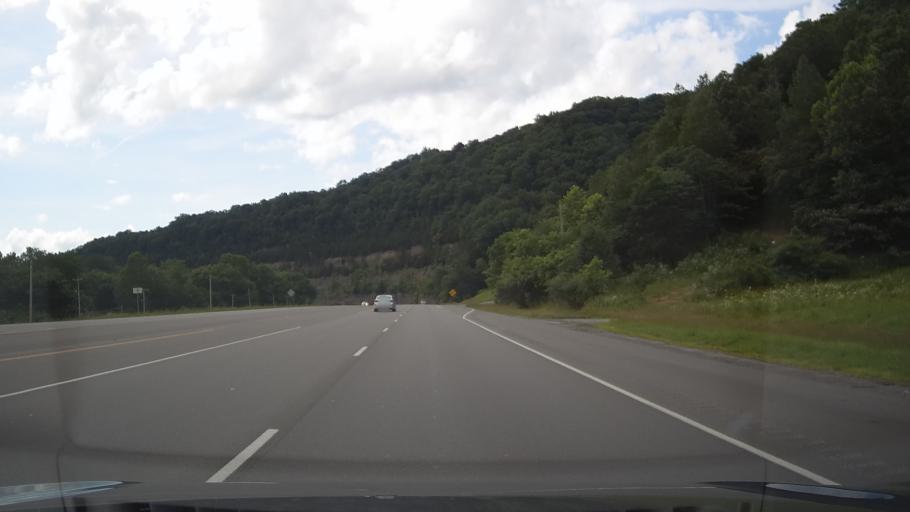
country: US
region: Kentucky
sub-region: Floyd County
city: Prestonsburg
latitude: 37.6000
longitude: -82.6844
